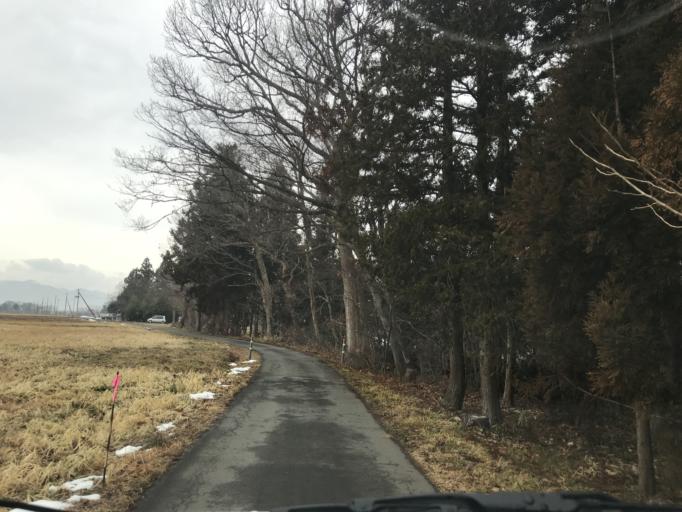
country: JP
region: Iwate
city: Mizusawa
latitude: 39.1834
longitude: 141.1390
